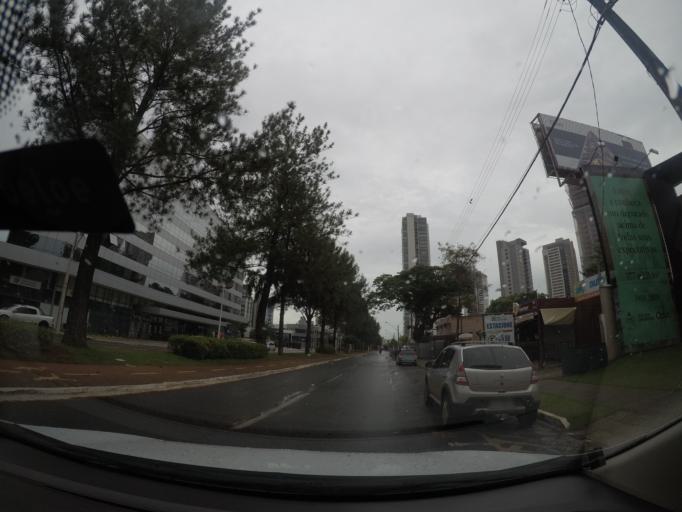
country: BR
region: Goias
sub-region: Goiania
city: Goiania
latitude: -16.7012
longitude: -49.2571
